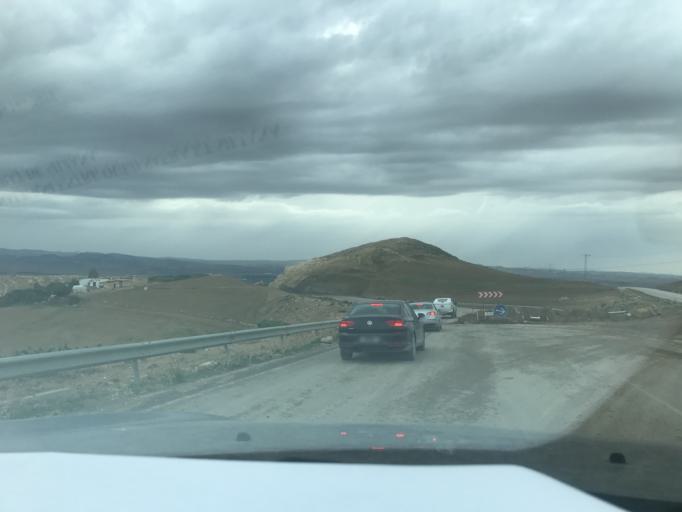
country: TN
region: Silyanah
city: Siliana
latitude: 36.0889
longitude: 9.4633
